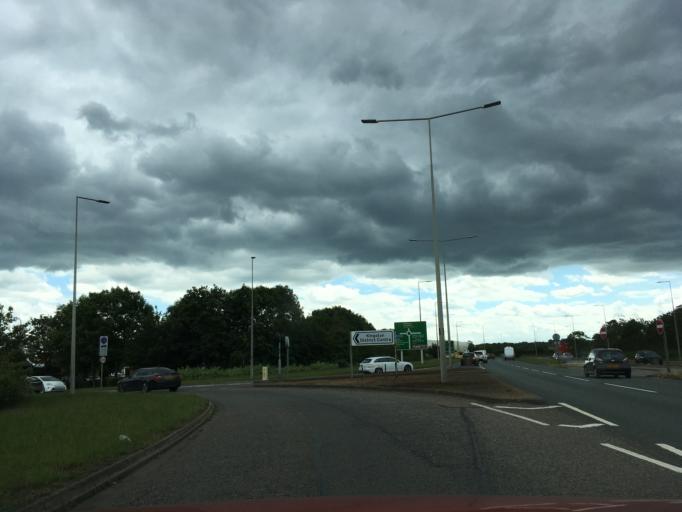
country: GB
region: England
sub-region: Milton Keynes
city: Broughton
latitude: 52.0364
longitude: -0.6918
